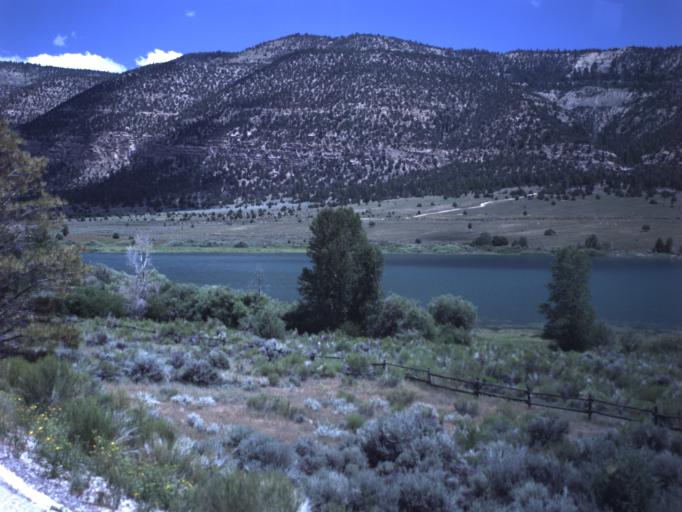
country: US
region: Utah
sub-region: Emery County
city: Orangeville
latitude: 39.3126
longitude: -111.2846
